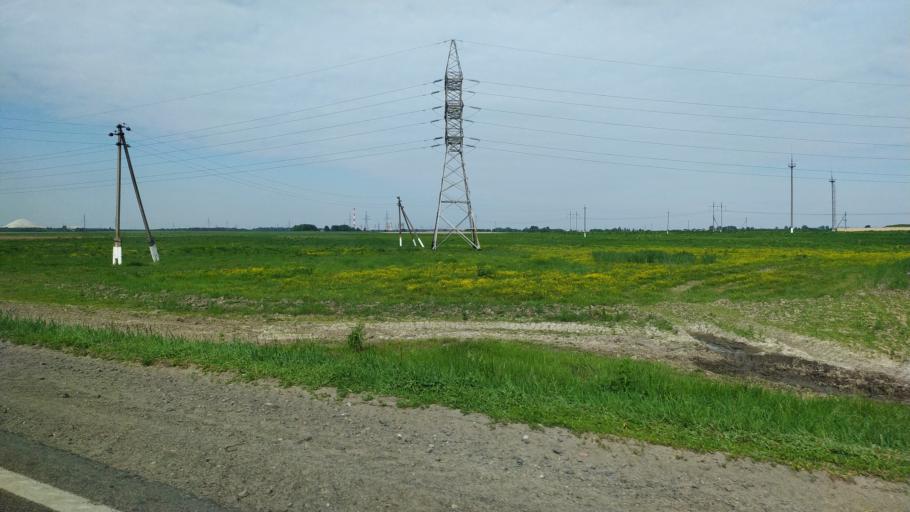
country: BY
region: Gomel
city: Gomel
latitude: 52.4553
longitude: 30.9002
